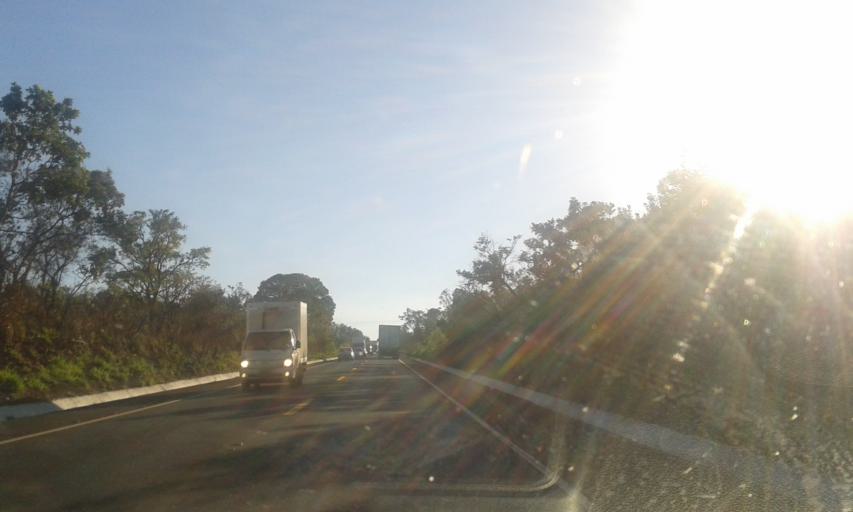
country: BR
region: Minas Gerais
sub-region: Monte Alegre De Minas
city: Monte Alegre de Minas
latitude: -18.8798
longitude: -49.1268
